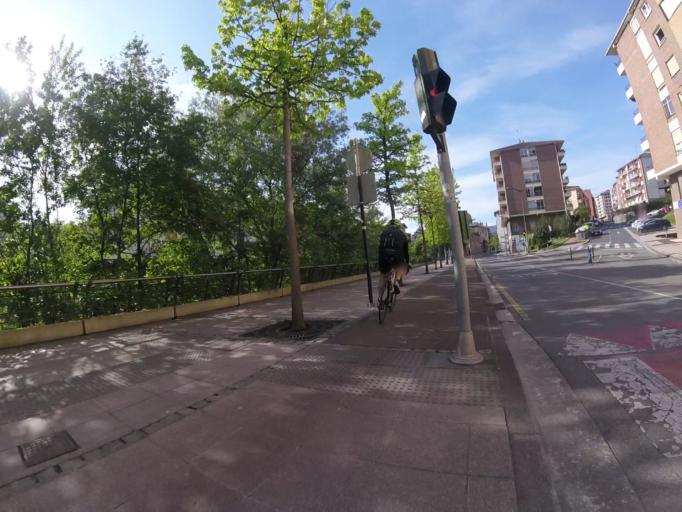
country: ES
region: Basque Country
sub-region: Provincia de Guipuzcoa
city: Beasain
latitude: 43.0516
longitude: -2.1898
